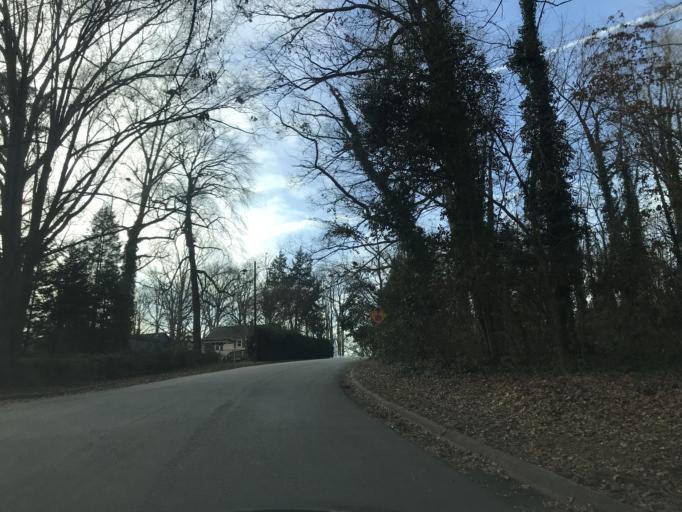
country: US
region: North Carolina
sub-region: Wake County
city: Raleigh
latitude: 35.7985
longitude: -78.6152
